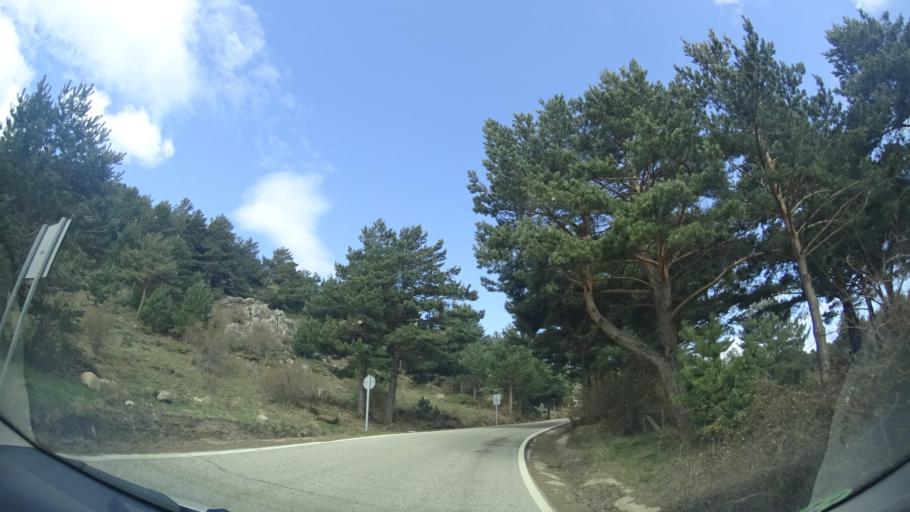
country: ES
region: Madrid
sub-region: Provincia de Madrid
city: Canencia
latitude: 40.8674
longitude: -3.7630
